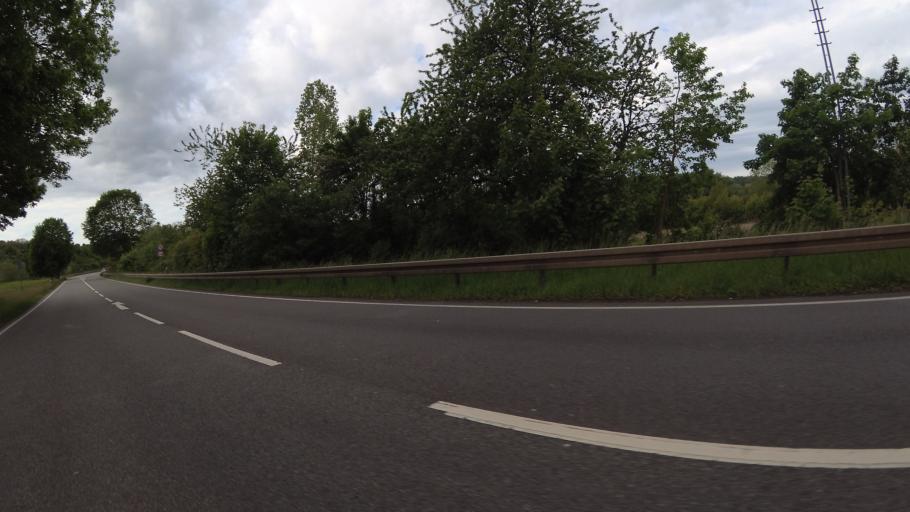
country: LU
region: Grevenmacher
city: Schengen
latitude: 49.4876
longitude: 6.3722
